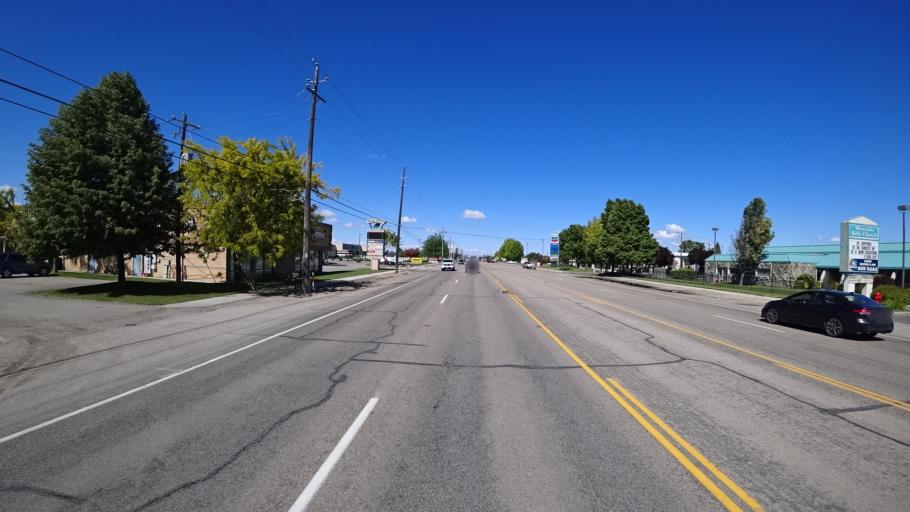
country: US
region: Idaho
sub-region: Ada County
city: Meridian
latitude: 43.6193
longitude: -116.3687
